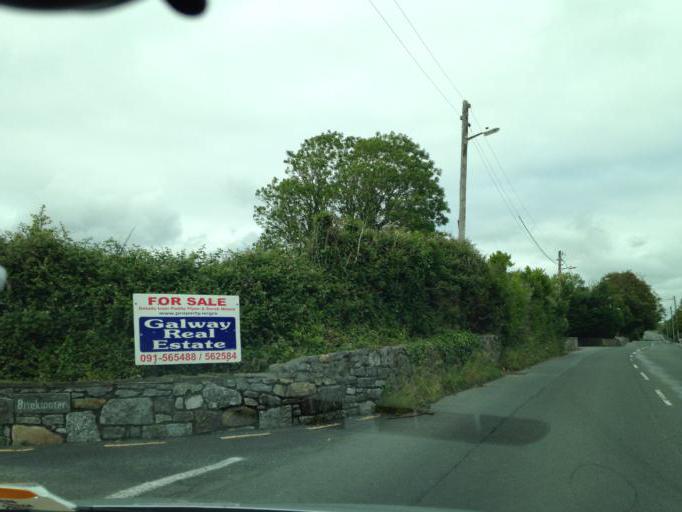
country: IE
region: Connaught
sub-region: County Galway
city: Gaillimh
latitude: 53.2865
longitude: -9.0561
